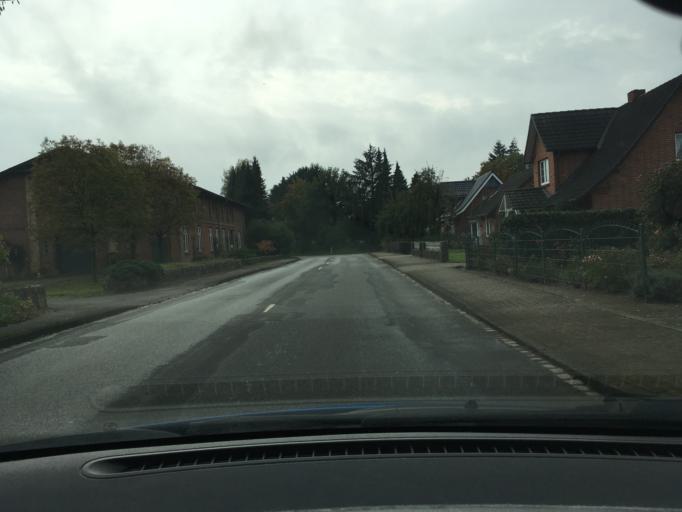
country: DE
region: Schleswig-Holstein
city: Blunk
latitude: 54.0072
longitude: 10.3154
